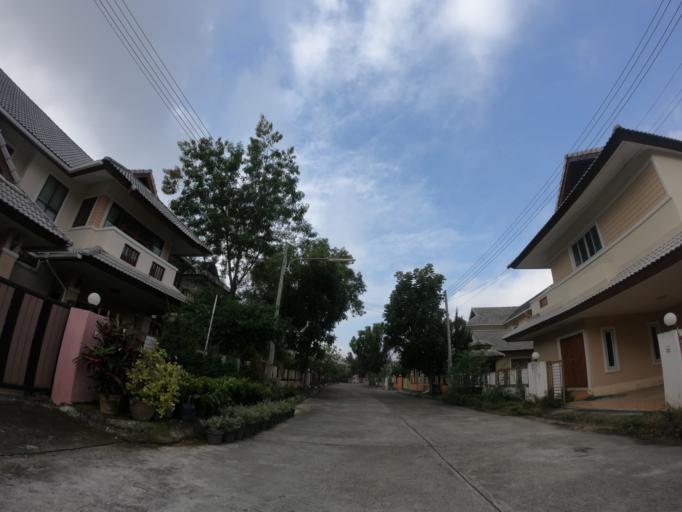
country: TH
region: Chiang Mai
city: Chiang Mai
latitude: 18.7562
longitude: 98.9773
